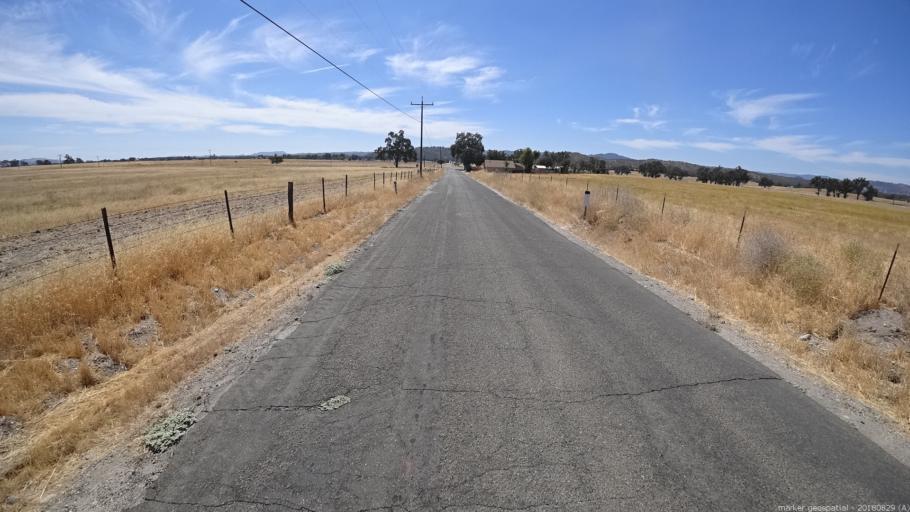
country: US
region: California
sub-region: Monterey County
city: King City
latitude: 35.9385
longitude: -121.0821
